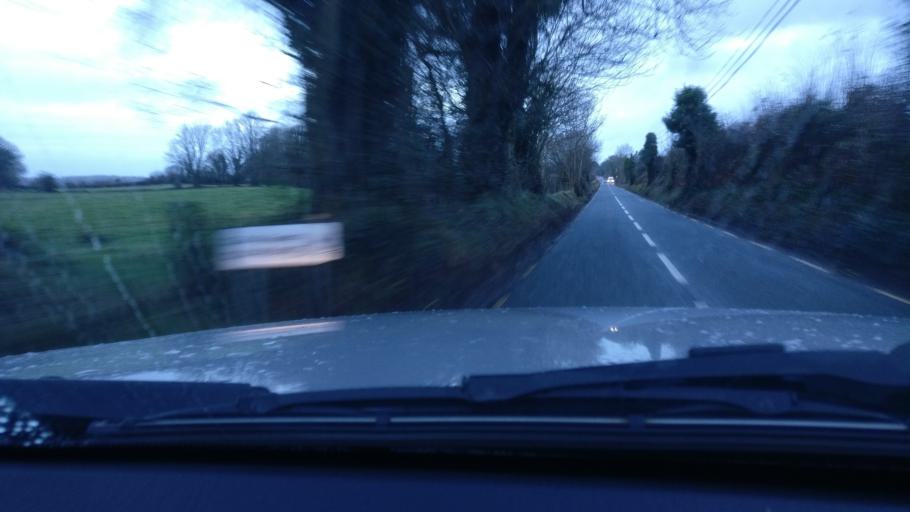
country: IE
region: Connaught
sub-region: County Galway
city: Ballinasloe
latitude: 53.2704
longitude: -8.2478
